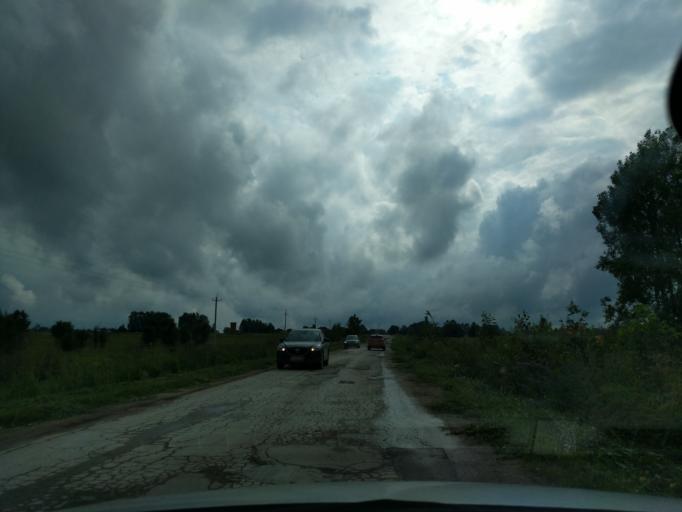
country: RU
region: Kaluga
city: Nikola-Lenivets
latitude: 54.7473
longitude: 35.6477
